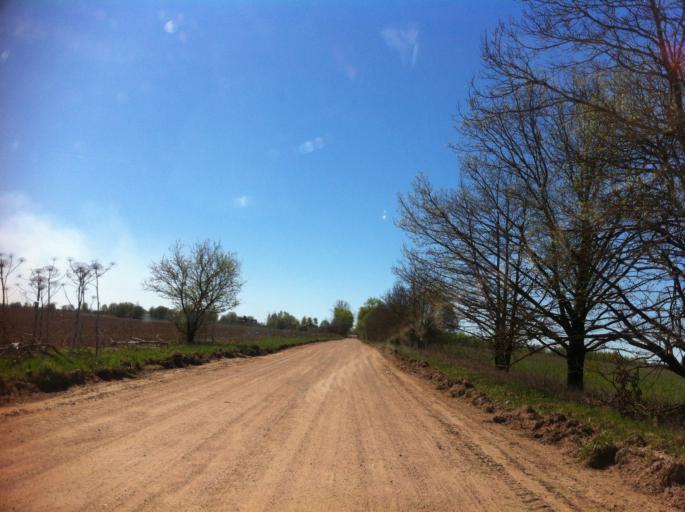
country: RU
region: Pskov
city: Izborsk
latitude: 57.7952
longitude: 27.9638
